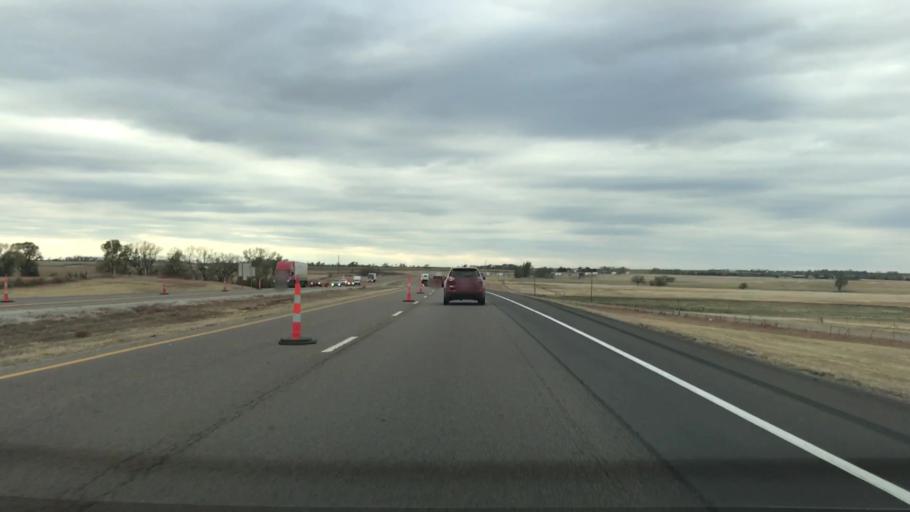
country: US
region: Oklahoma
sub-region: Beckham County
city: Elk City
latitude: 35.4248
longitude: -99.2950
